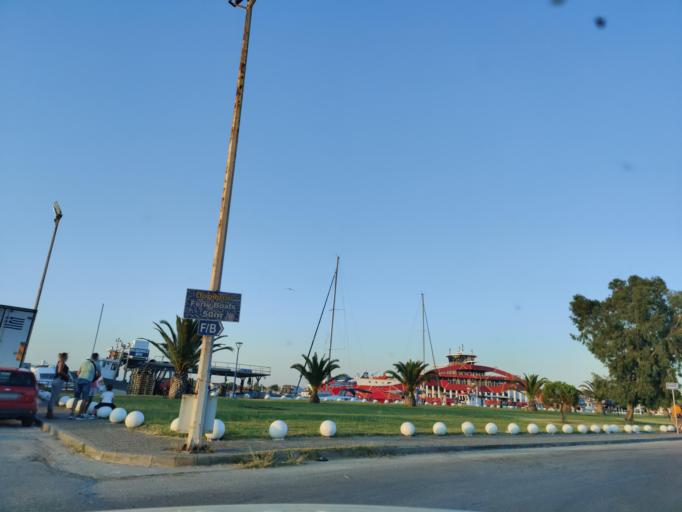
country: GR
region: East Macedonia and Thrace
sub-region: Nomos Kavalas
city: Keramoti
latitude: 40.8563
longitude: 24.6993
